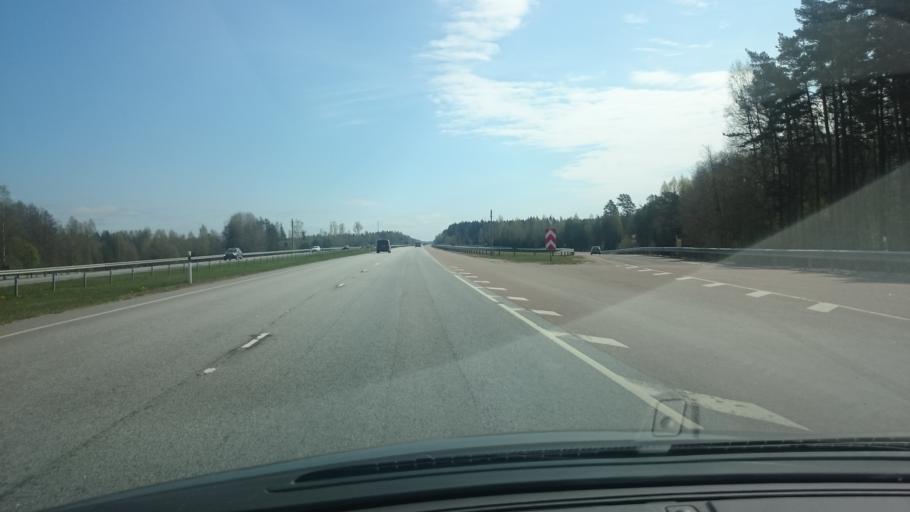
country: EE
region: Harju
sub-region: Kuusalu vald
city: Kuusalu
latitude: 59.4557
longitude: 25.5129
